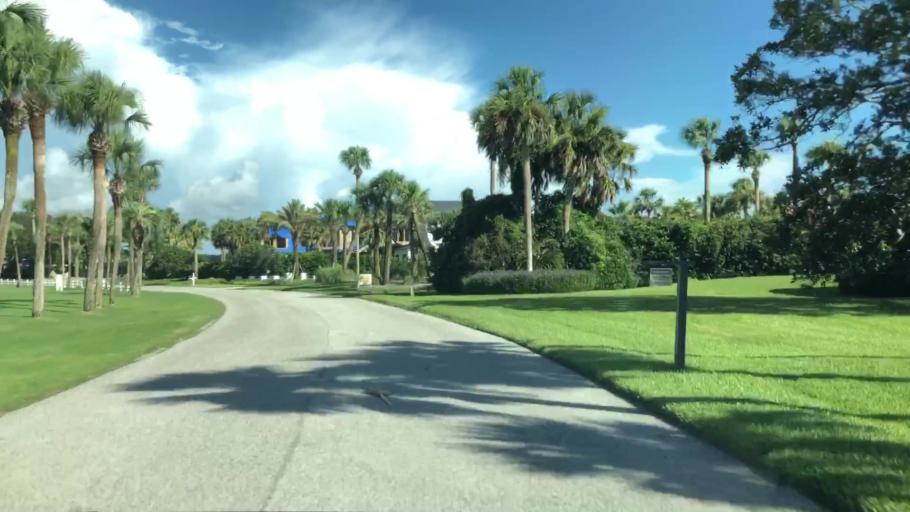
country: US
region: Florida
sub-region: Saint Johns County
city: Ponte Vedra Beach
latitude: 30.2420
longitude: -81.3818
